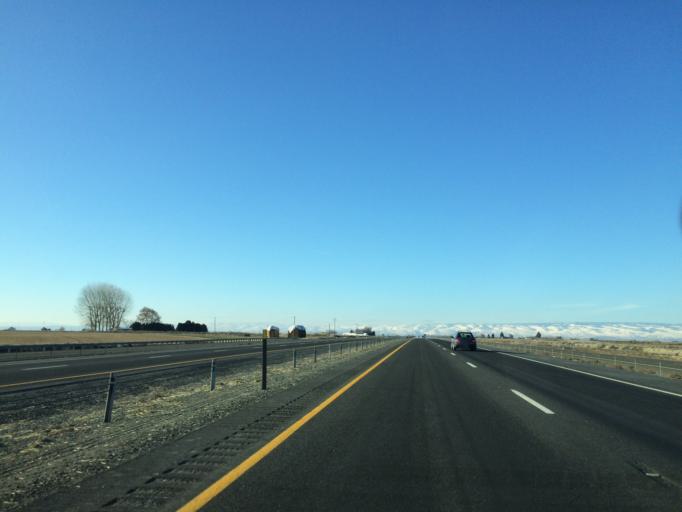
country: US
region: Washington
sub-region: Grant County
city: Quincy
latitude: 47.1035
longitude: -119.7852
